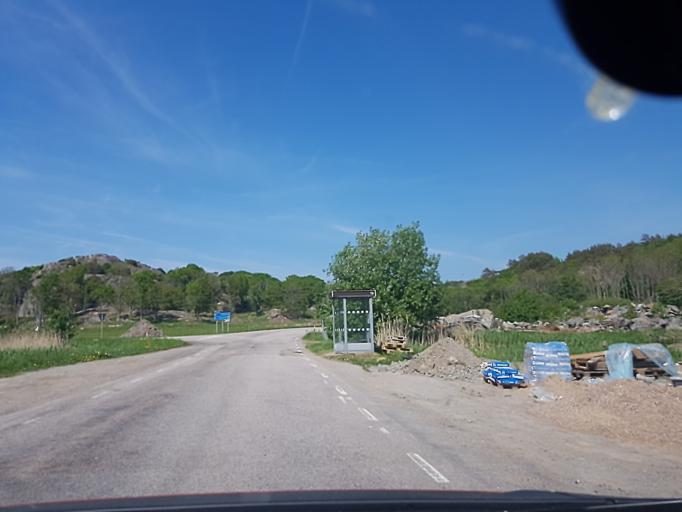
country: SE
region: Vaestra Goetaland
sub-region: Lysekils Kommun
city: Lysekil
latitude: 58.1581
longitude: 11.4614
